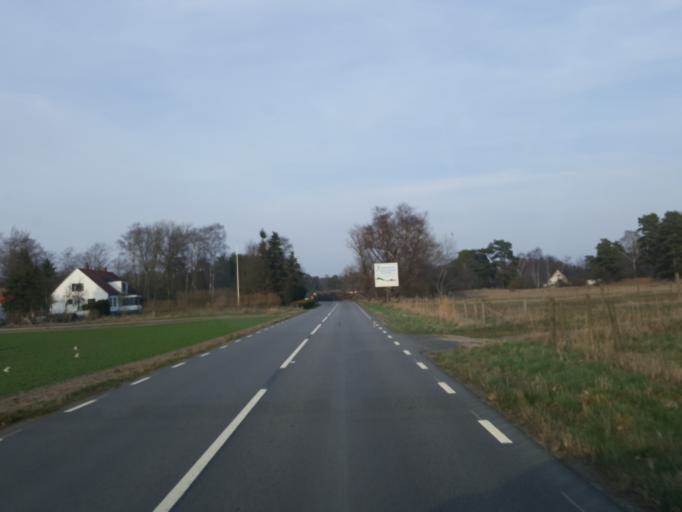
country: SE
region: Skane
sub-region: Simrishamns Kommun
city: Simrishamn
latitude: 55.4139
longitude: 14.2028
